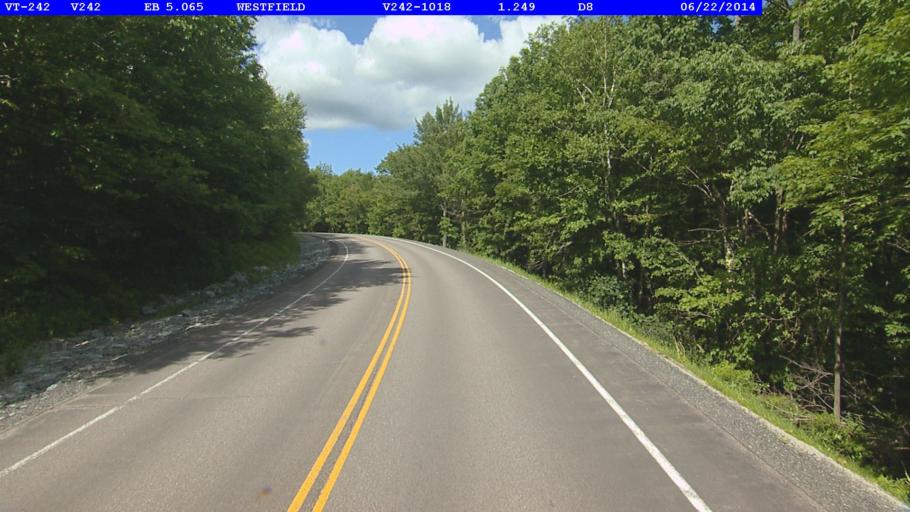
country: US
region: Vermont
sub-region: Franklin County
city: Richford
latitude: 44.8979
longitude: -72.5184
